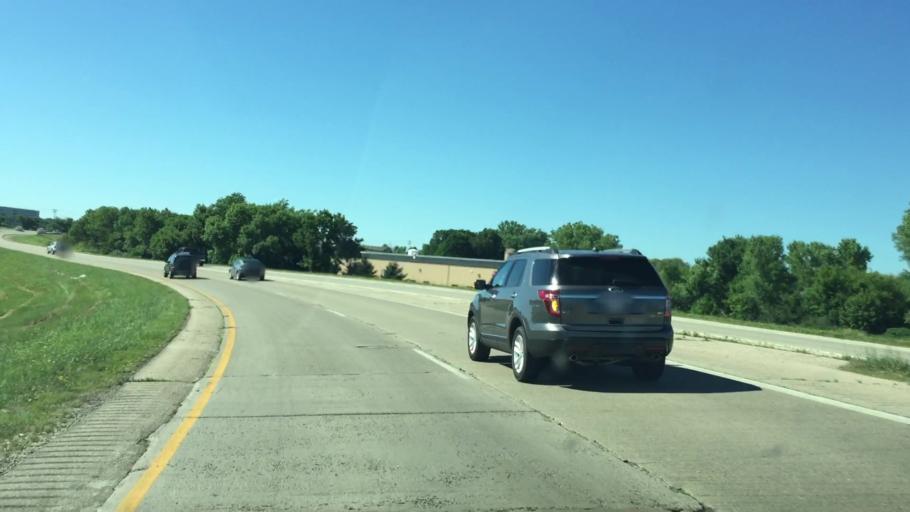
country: US
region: Wisconsin
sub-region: Dane County
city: McFarland
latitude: 43.0488
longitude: -89.2734
